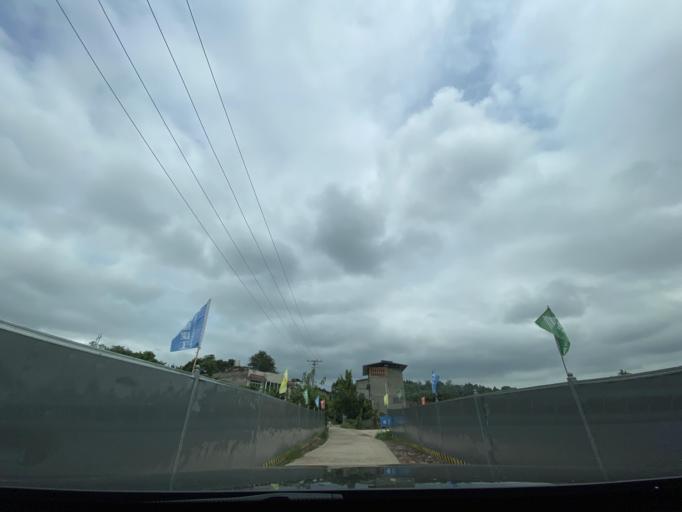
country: CN
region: Sichuan
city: Jiancheng
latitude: 30.4020
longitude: 104.5705
